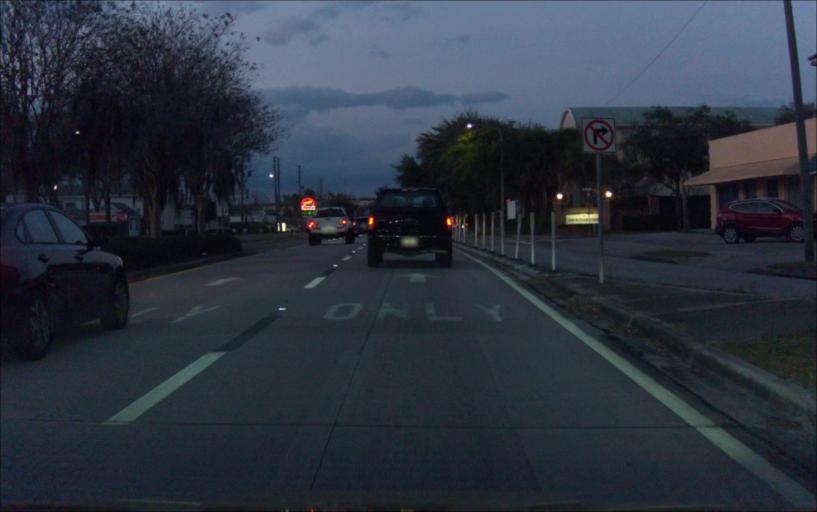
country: US
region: Florida
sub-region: Orange County
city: Maitland
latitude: 28.6183
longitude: -81.3643
